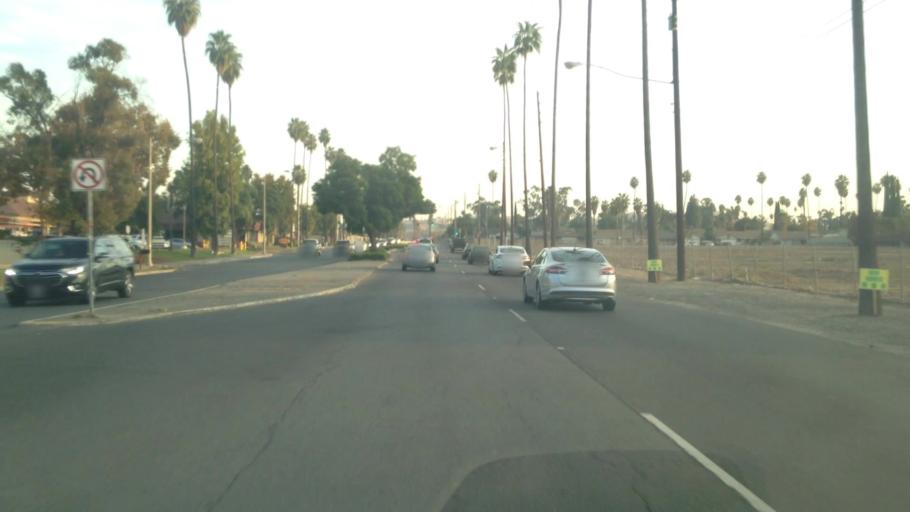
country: US
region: California
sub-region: Riverside County
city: Riverside
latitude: 33.9101
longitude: -117.4382
